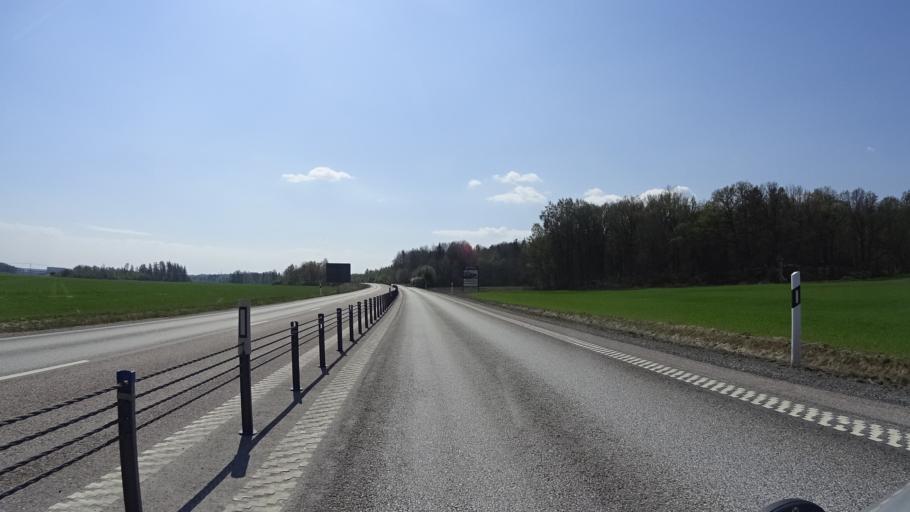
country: SE
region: Vaestmanland
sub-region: Arboga Kommun
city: Arboga
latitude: 59.4216
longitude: 15.8870
